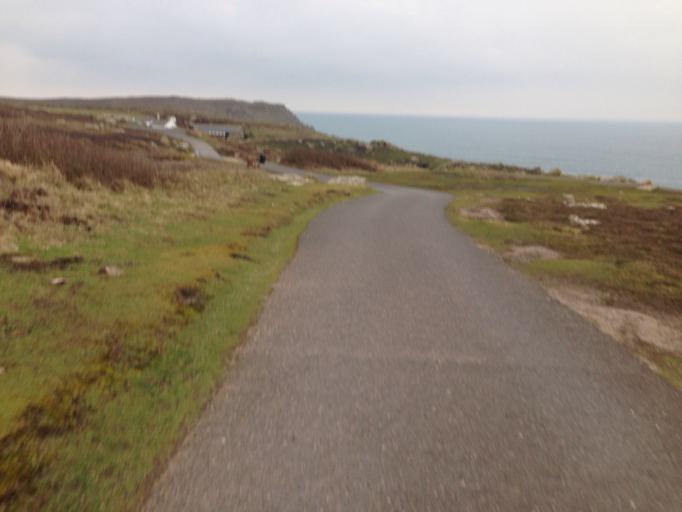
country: GB
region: England
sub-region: Cornwall
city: Sennen
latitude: 50.0645
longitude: -5.7121
